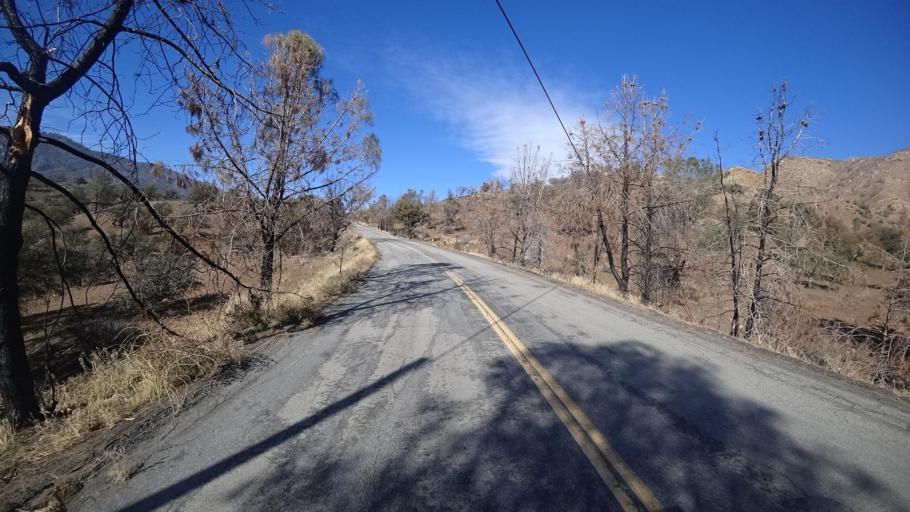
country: US
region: California
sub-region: Kern County
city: Bodfish
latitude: 35.4461
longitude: -118.5284
